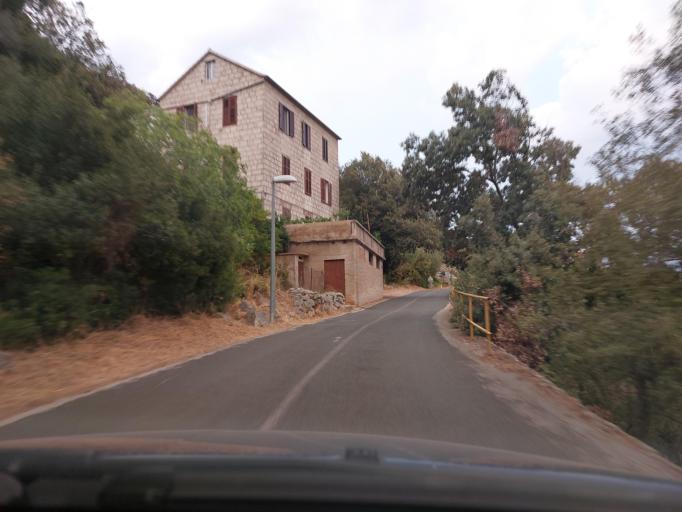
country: HR
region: Dubrovacko-Neretvanska
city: Smokvica
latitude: 42.7683
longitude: 16.8932
